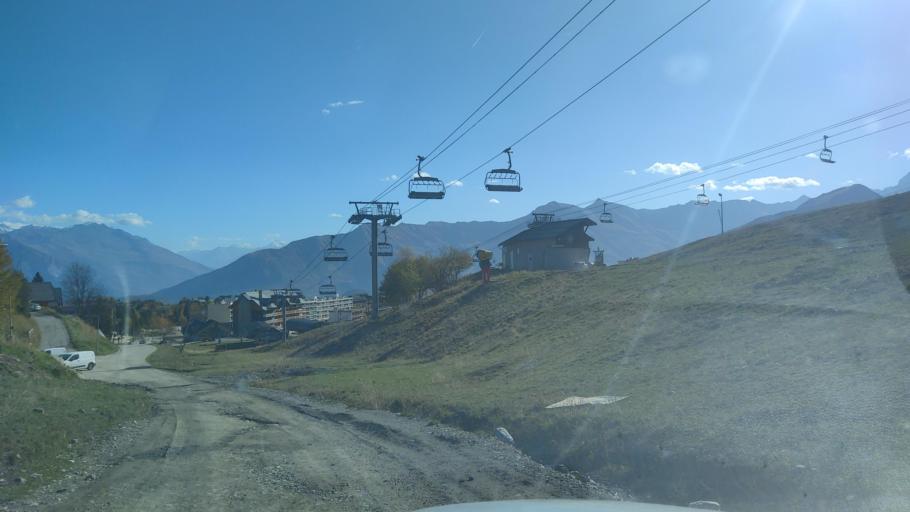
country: FR
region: Rhone-Alpes
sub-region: Departement de la Savoie
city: Saint-Etienne-de-Cuines
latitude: 45.2563
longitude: 6.2528
